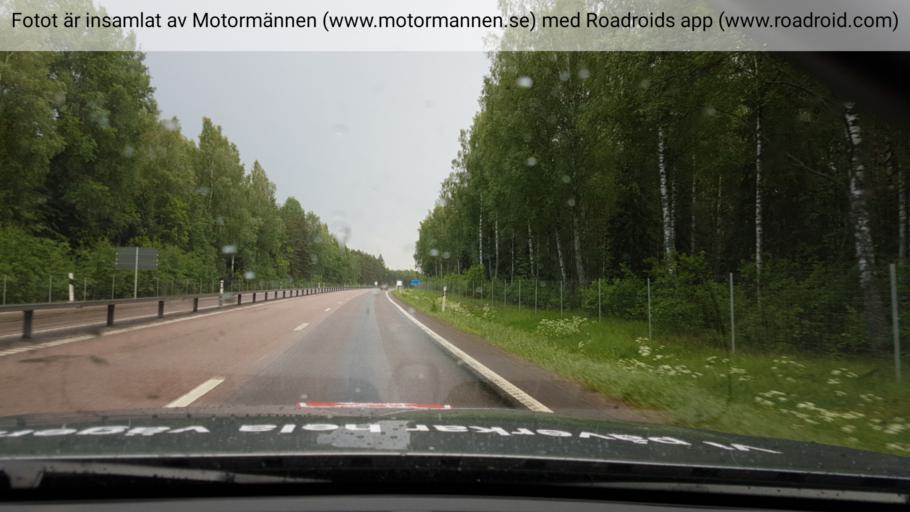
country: SE
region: Vaestmanland
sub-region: Vasteras
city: Hokasen
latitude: 59.6727
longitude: 16.5825
